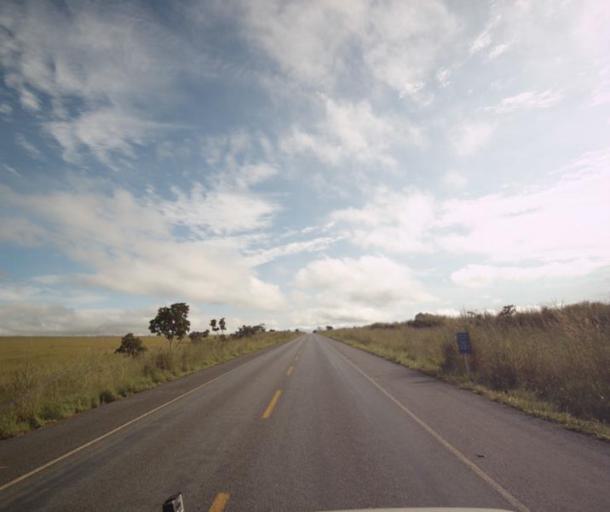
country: BR
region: Goias
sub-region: Padre Bernardo
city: Padre Bernardo
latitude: -15.4717
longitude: -48.6147
